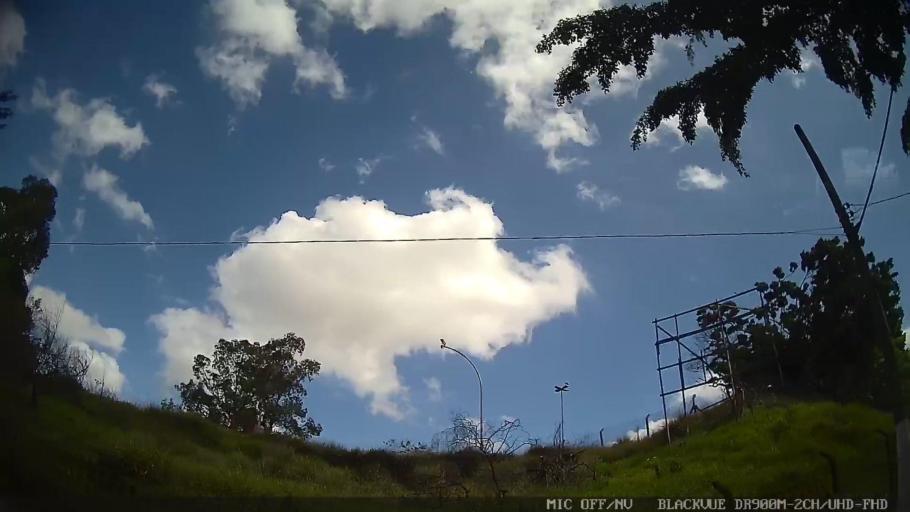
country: BR
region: Sao Paulo
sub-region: Sao Caetano Do Sul
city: Sao Caetano do Sul
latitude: -23.6481
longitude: -46.5878
